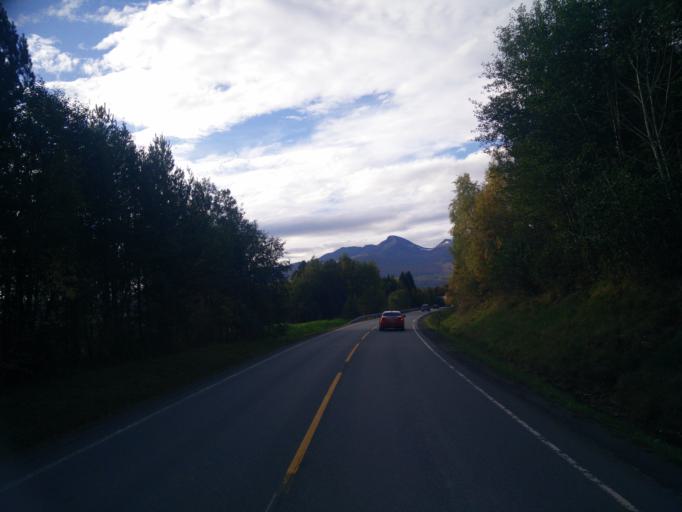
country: NO
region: More og Romsdal
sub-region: Vestnes
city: Vestnes
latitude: 62.6420
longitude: 7.0814
